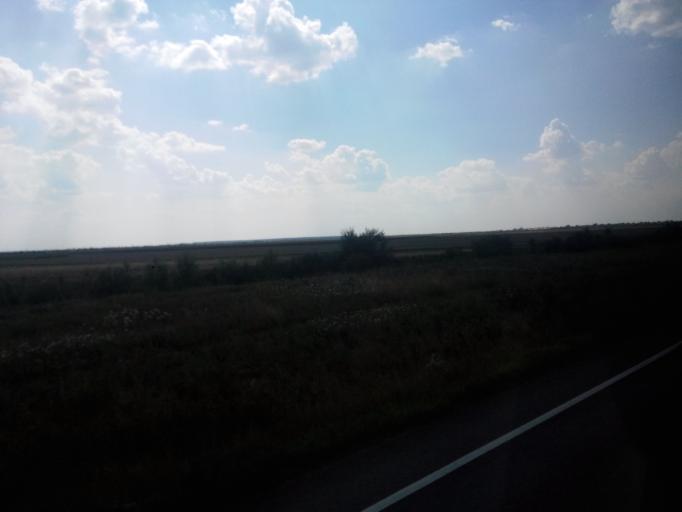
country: RO
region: Timis
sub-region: Comuna Topolovatu Mare
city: Topolovatu Mare
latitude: 45.7790
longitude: 21.6091
